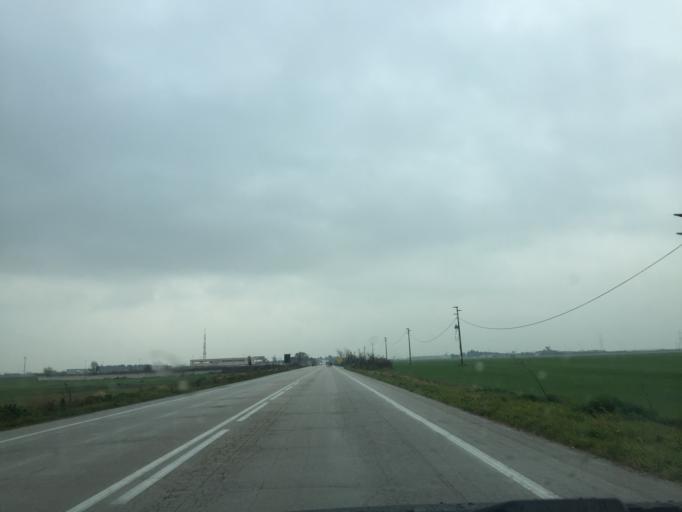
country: IT
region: Apulia
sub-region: Provincia di Foggia
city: Foggia
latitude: 41.4832
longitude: 15.5186
